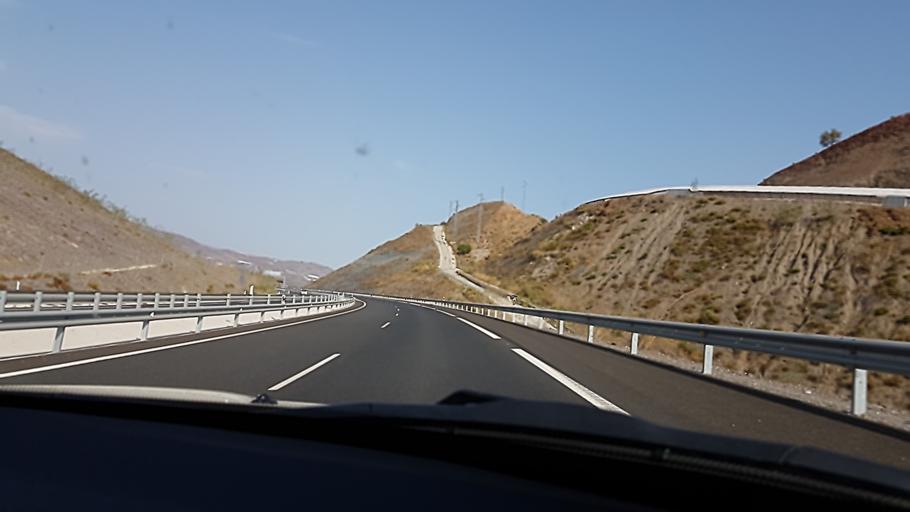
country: ES
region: Andalusia
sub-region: Provincia de Granada
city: Polopos
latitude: 36.7511
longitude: -3.2855
